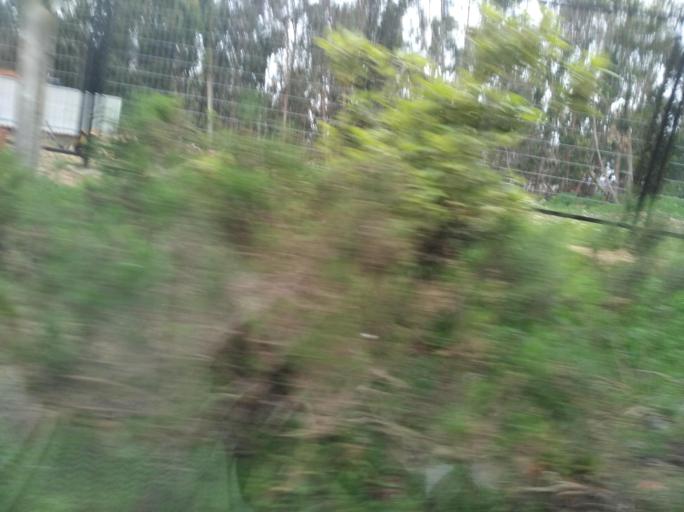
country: CL
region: Valparaiso
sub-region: Provincia de Valparaiso
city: Valparaiso
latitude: -33.1043
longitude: -71.6724
